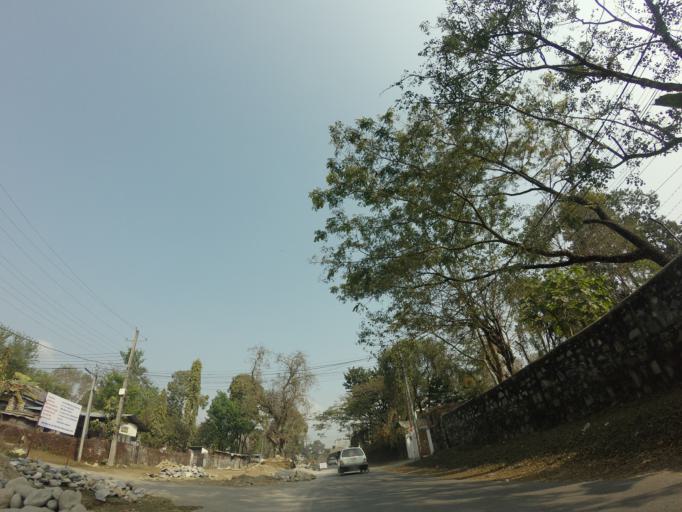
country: NP
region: Western Region
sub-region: Gandaki Zone
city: Pokhara
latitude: 28.2048
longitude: 83.9719
